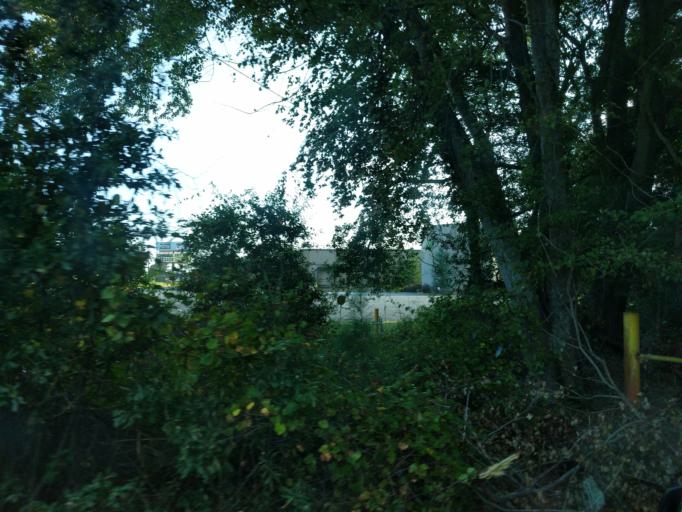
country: US
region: South Carolina
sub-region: Anderson County
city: Piedmont
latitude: 34.7046
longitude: -82.5016
